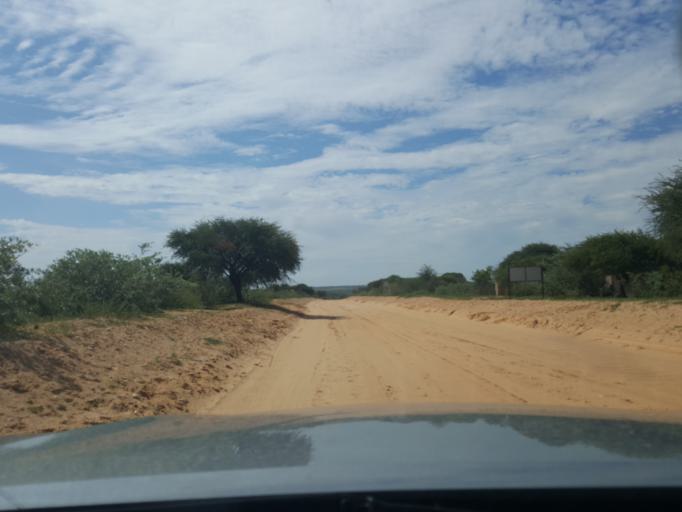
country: BW
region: Kweneng
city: Letlhakeng
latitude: -24.0763
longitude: 25.0297
